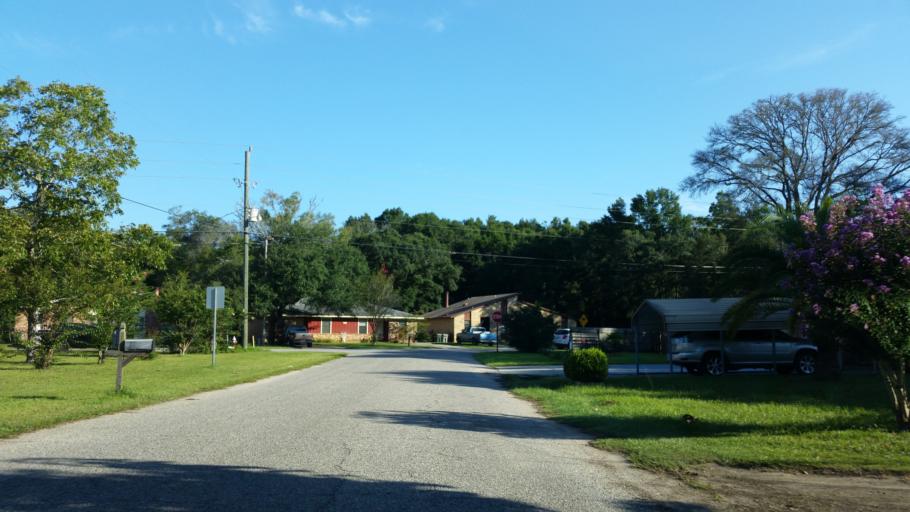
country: US
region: Florida
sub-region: Escambia County
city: Bellview
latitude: 30.4426
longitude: -87.3166
